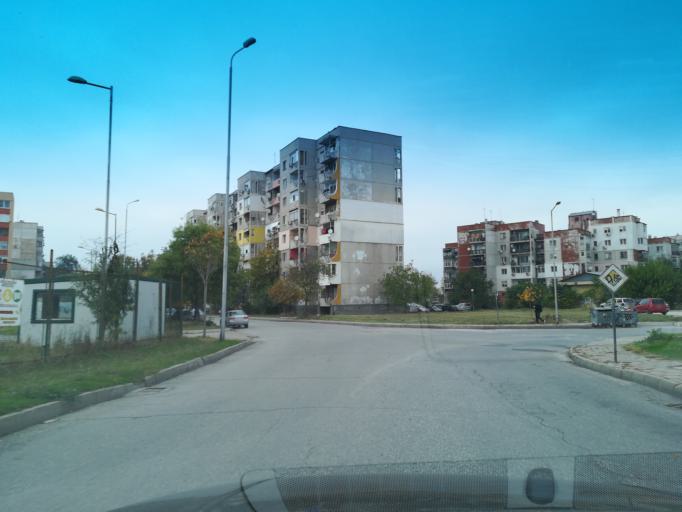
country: BG
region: Plovdiv
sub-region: Obshtina Plovdiv
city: Plovdiv
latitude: 42.1441
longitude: 24.7987
